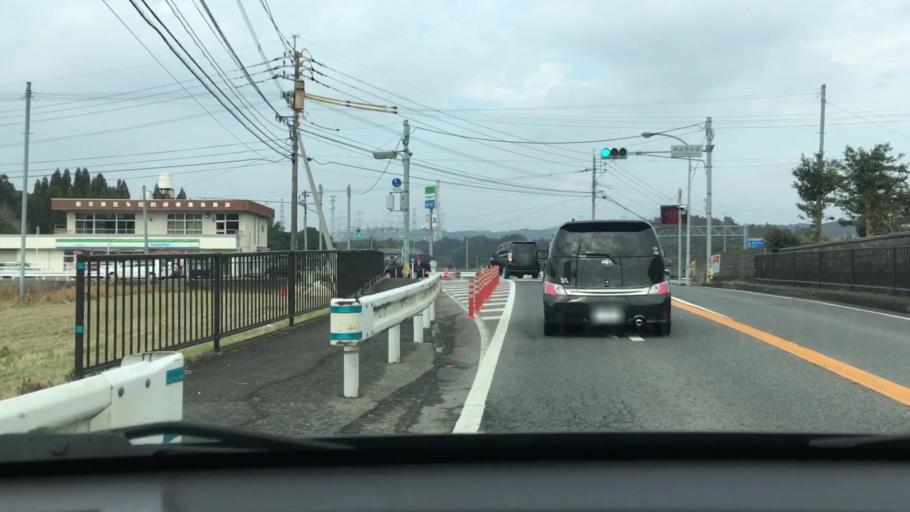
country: JP
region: Saga Prefecture
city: Imaricho-ko
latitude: 33.3376
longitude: 129.9312
